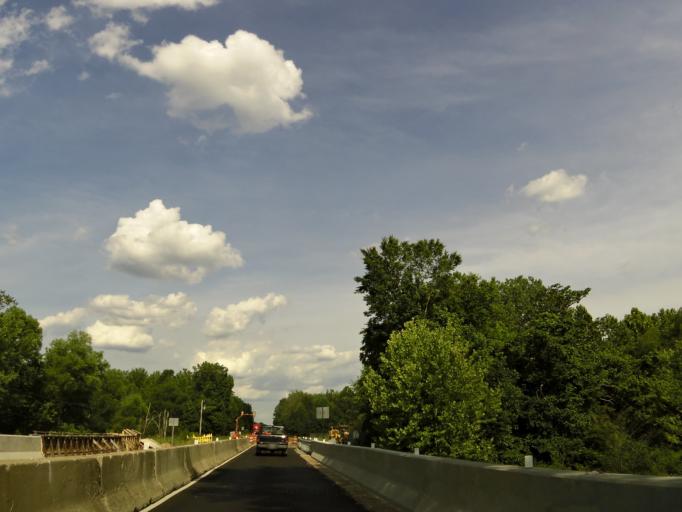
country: US
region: Tennessee
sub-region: Carroll County
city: Bruceton
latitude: 36.0376
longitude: -88.2347
